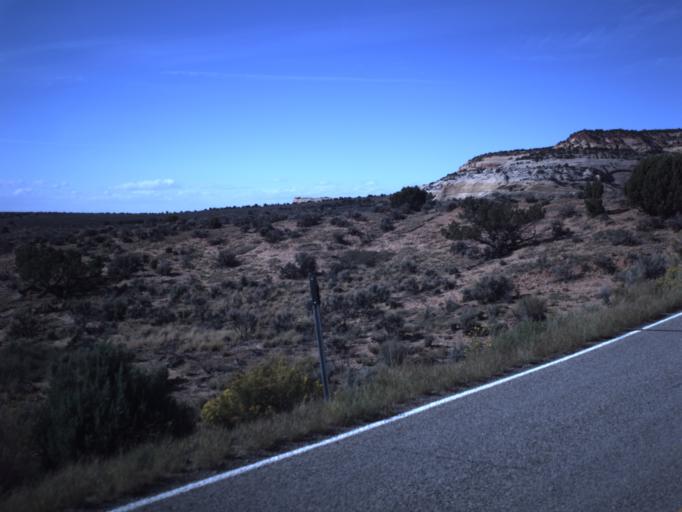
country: US
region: Utah
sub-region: San Juan County
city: Monticello
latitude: 38.0555
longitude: -109.4086
